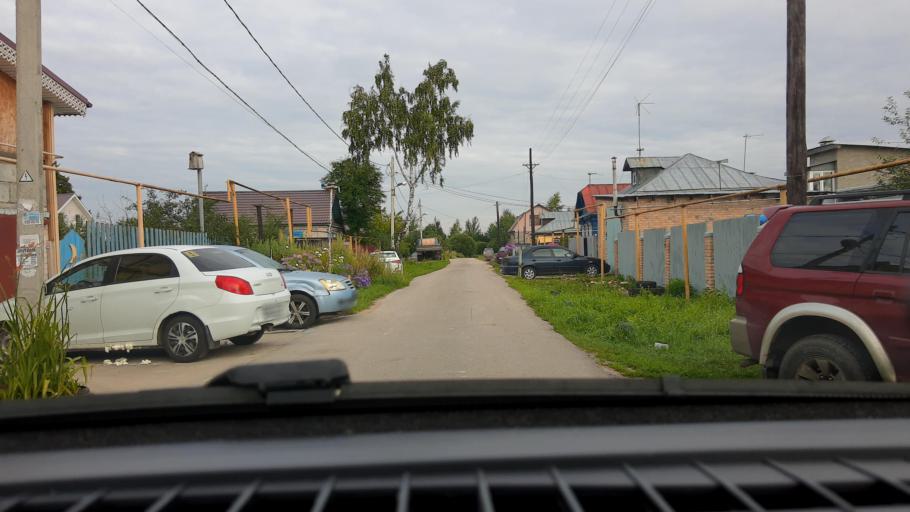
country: RU
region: Nizjnij Novgorod
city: Gorbatovka
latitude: 56.2751
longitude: 43.8758
